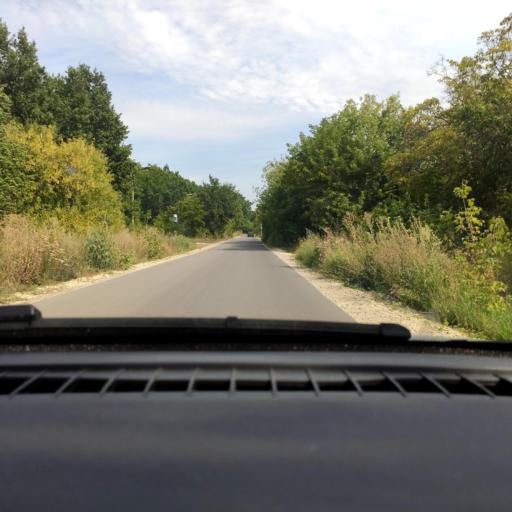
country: RU
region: Voronezj
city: Pridonskoy
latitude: 51.7379
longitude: 39.0663
